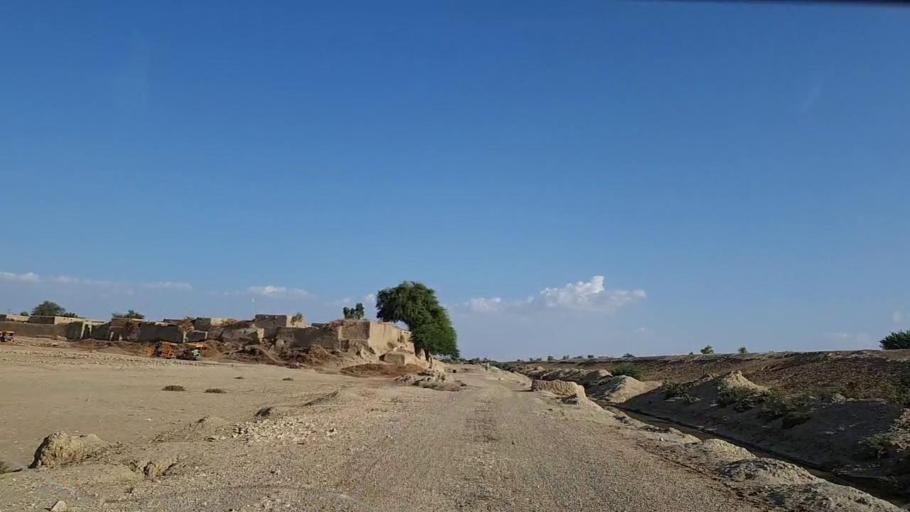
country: PK
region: Sindh
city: Johi
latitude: 26.5851
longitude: 67.5419
